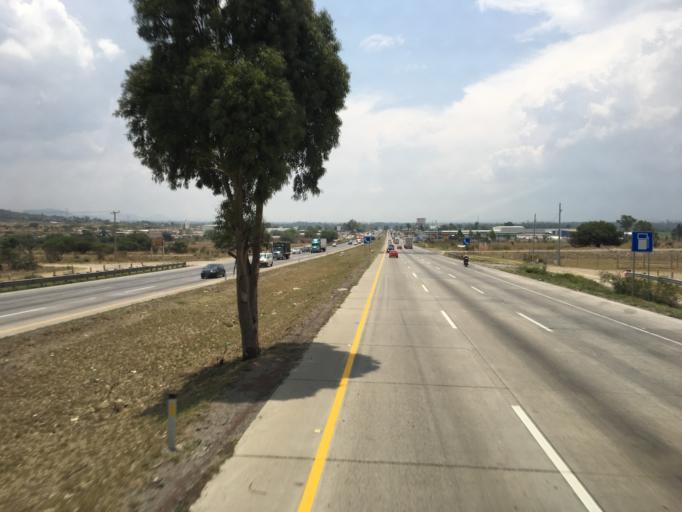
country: MX
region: Queretaro
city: La Estancia
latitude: 20.4138
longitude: -100.0414
